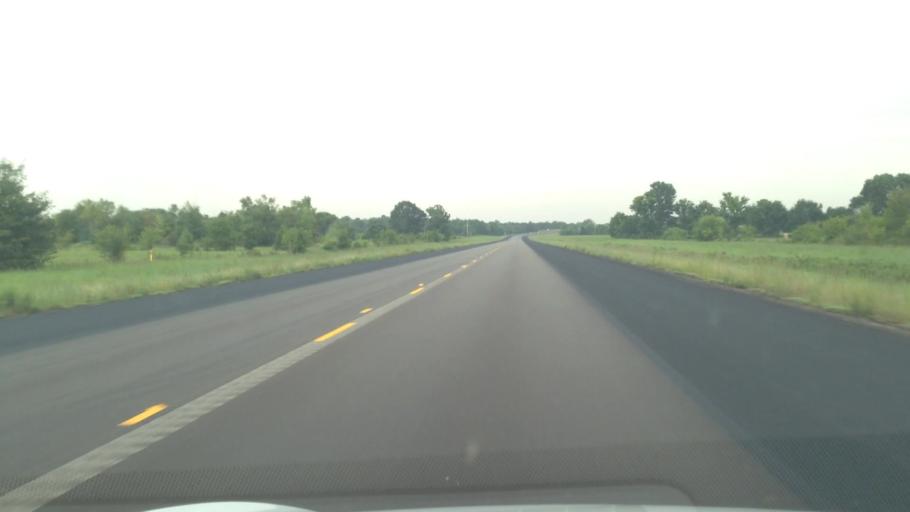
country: US
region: Kansas
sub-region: Cherokee County
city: Baxter Springs
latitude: 37.0341
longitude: -94.7062
